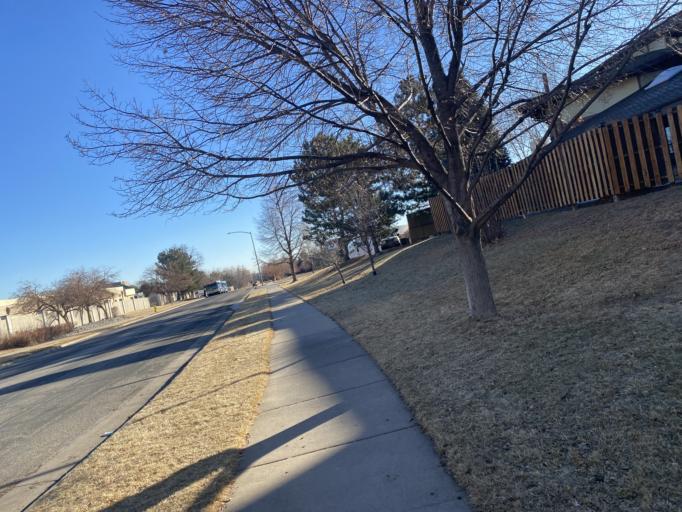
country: US
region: Colorado
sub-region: Jefferson County
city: Arvada
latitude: 39.8109
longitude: -105.1420
